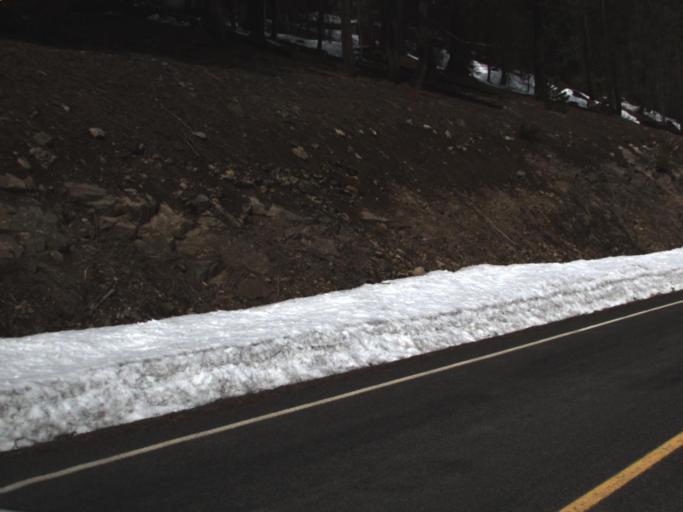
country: US
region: Washington
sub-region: Kittitas County
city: Cle Elum
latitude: 46.9285
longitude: -121.3624
